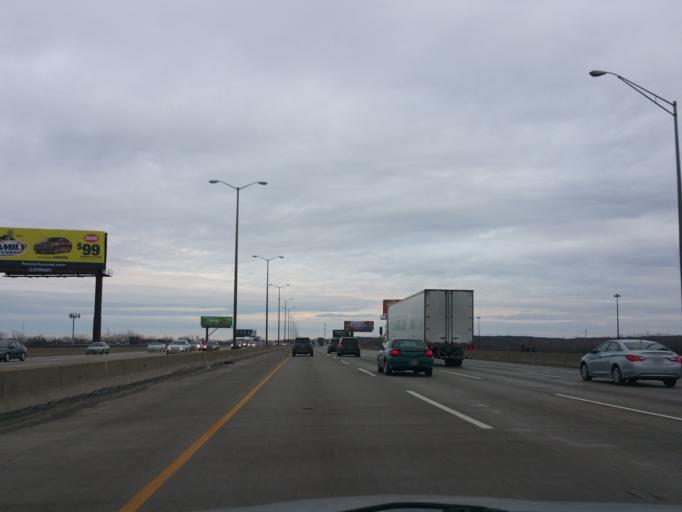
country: US
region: Illinois
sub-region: Cook County
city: Willow Springs
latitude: 41.7535
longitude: -87.8716
